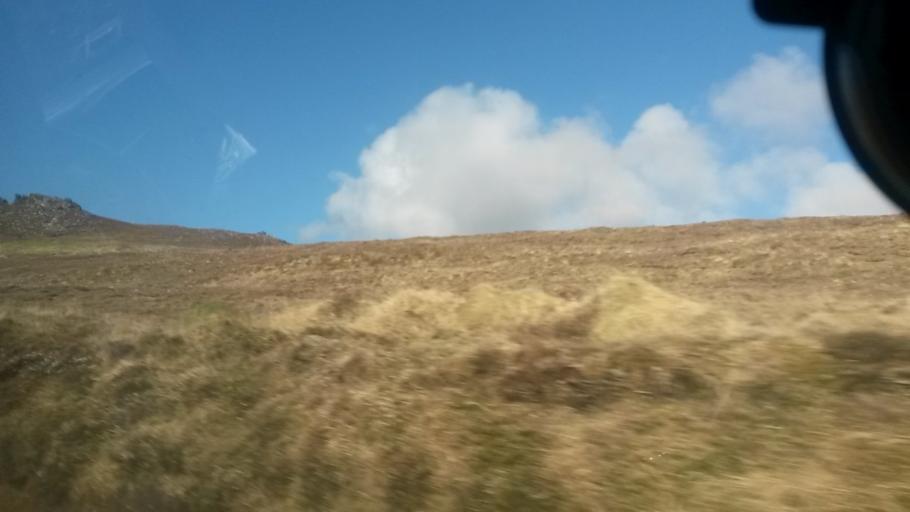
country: IE
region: Munster
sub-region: Ciarrai
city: Dingle
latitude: 52.1428
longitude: -10.4634
